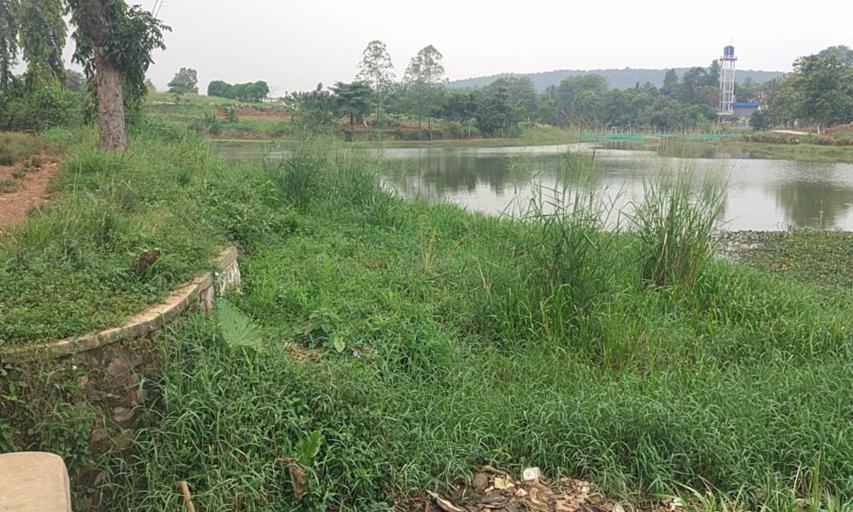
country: ID
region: West Java
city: Ciampea
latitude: -6.4955
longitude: 106.7456
